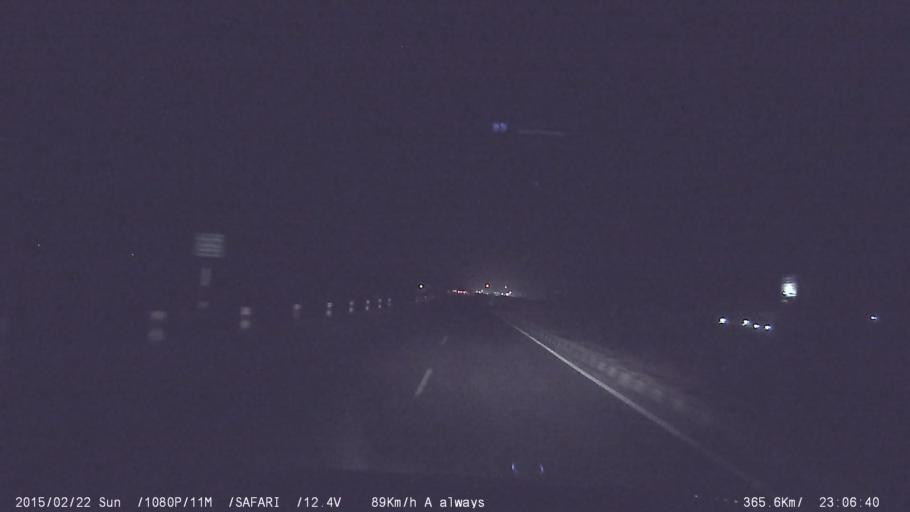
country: IN
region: Tamil Nadu
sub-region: Namakkal
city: Rasipuram
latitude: 11.4307
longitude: 78.1561
